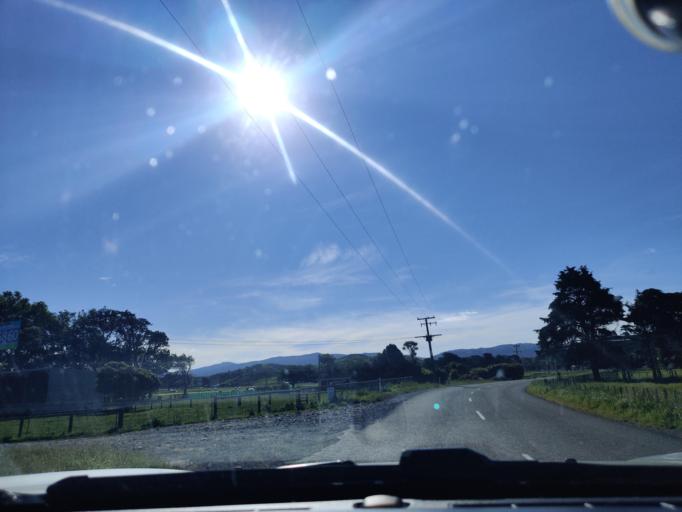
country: NZ
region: Manawatu-Wanganui
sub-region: Palmerston North City
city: Palmerston North
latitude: -40.5201
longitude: 175.7586
